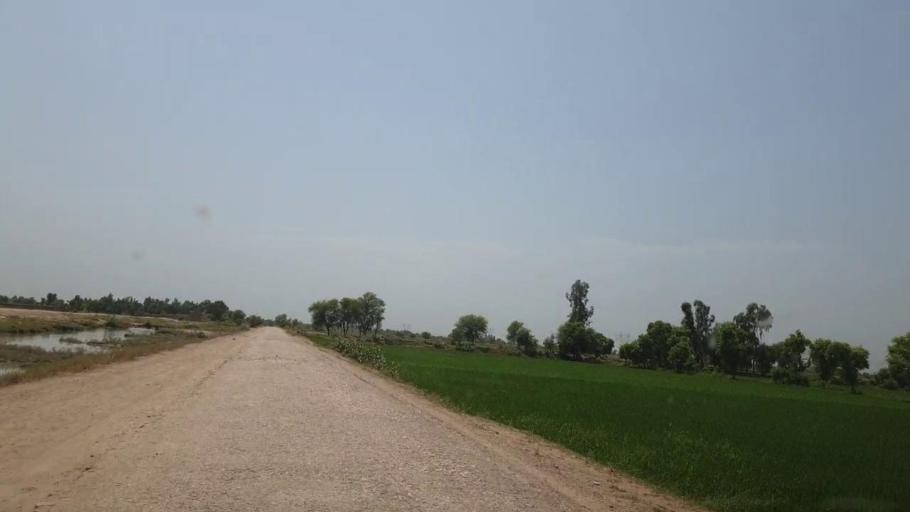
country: PK
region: Sindh
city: Lakhi
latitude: 27.8721
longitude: 68.6150
